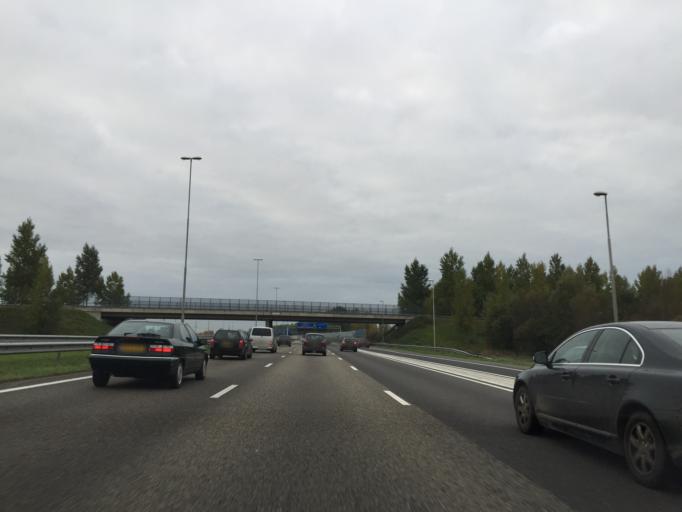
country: NL
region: South Holland
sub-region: Gemeente Strijen
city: Strijen
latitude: 51.6963
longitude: 4.6515
